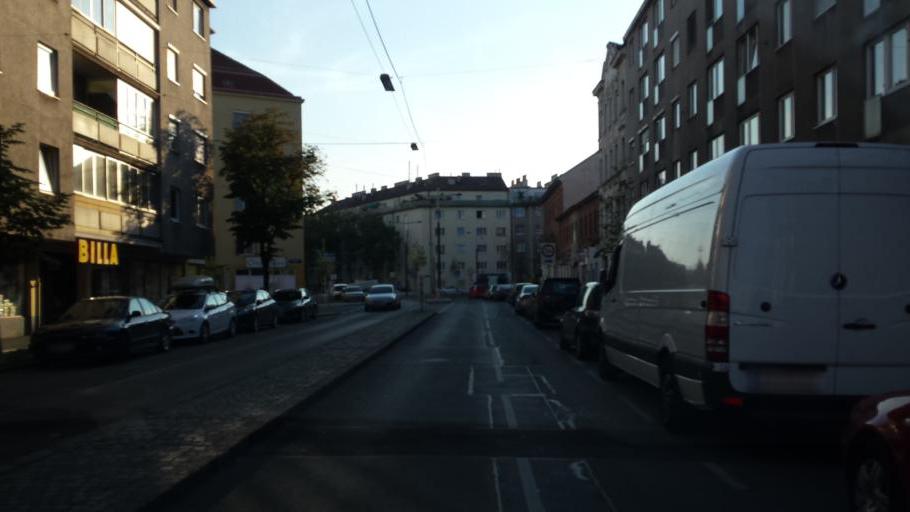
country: AT
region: Vienna
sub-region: Wien Stadt
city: Vienna
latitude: 48.2580
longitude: 16.4060
